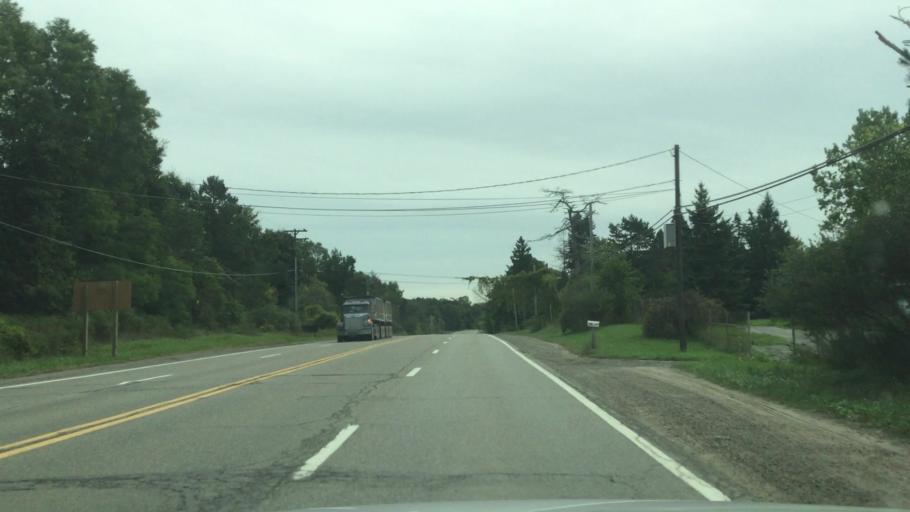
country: US
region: Michigan
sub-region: Oakland County
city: Holly
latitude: 42.8136
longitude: -83.5439
